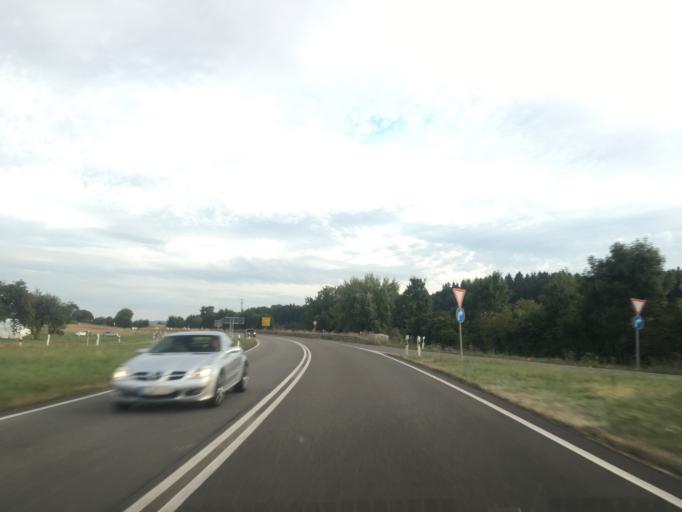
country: DE
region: Baden-Wuerttemberg
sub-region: Regierungsbezirk Stuttgart
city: Neckartailfingen
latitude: 48.6190
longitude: 9.2482
